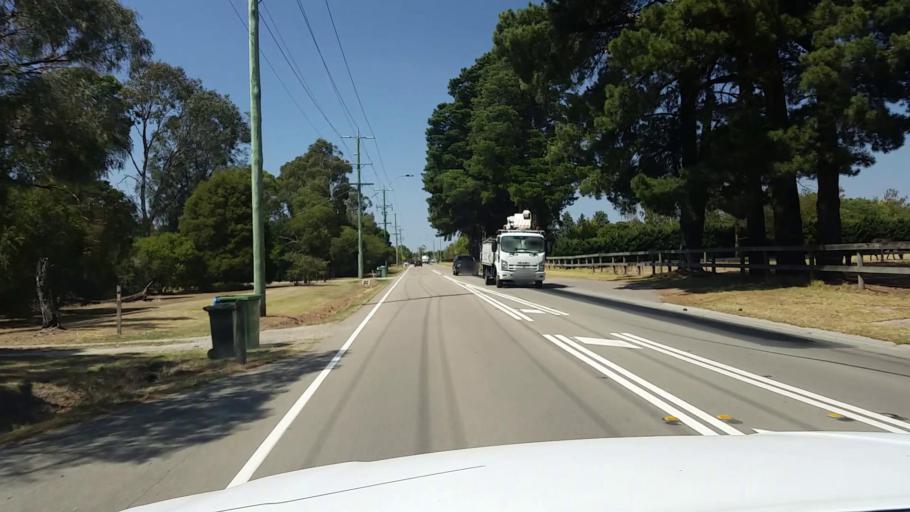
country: AU
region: Victoria
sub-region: Mornington Peninsula
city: Tyabb
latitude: -38.2379
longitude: 145.1682
